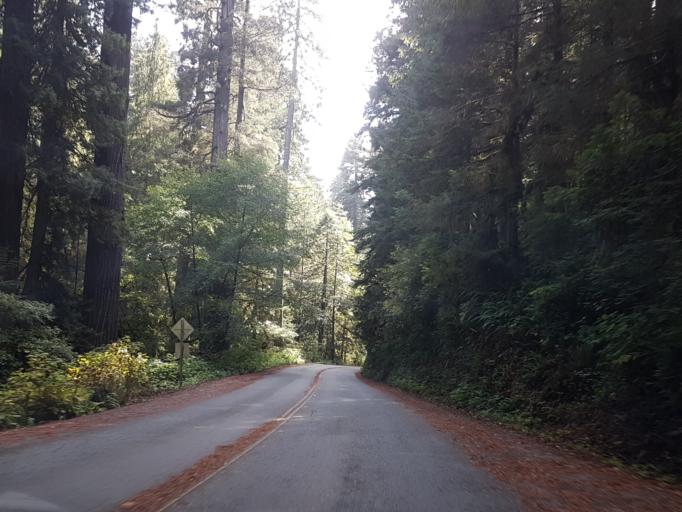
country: US
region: California
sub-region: Del Norte County
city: Bertsch-Oceanview
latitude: 41.4432
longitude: -124.0412
